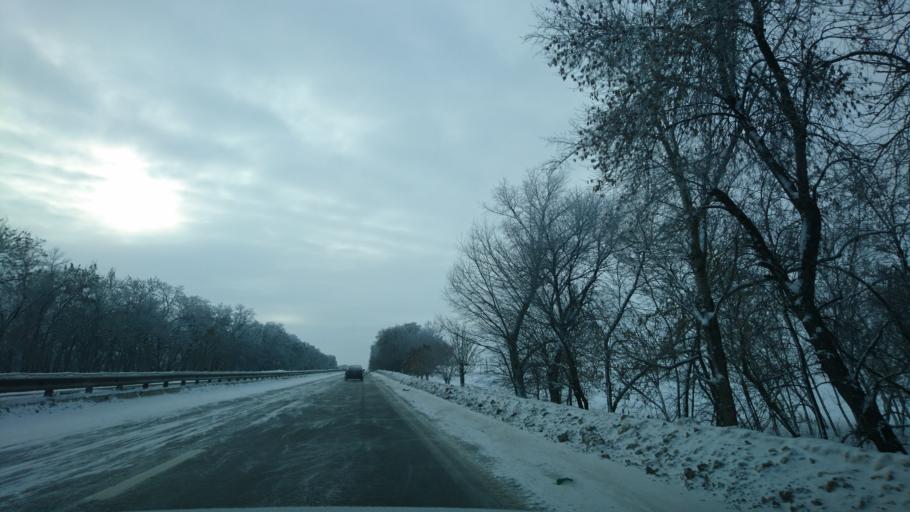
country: RU
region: Belgorod
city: Mayskiy
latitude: 50.4797
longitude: 36.4060
